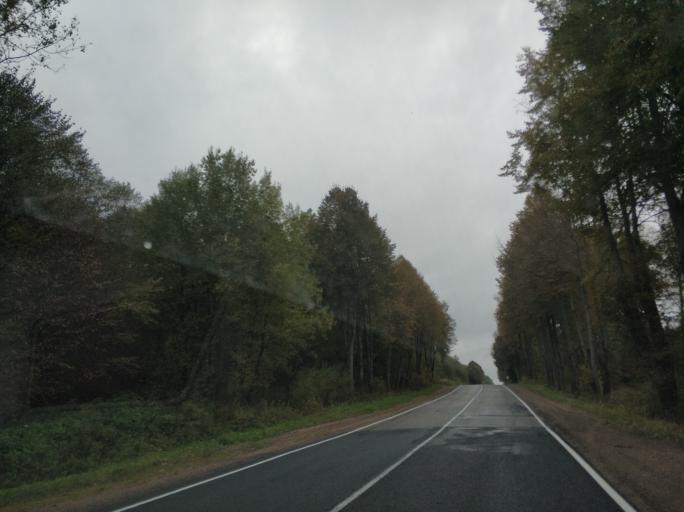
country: RU
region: Pskov
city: Opochka
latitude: 56.5575
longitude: 28.6306
